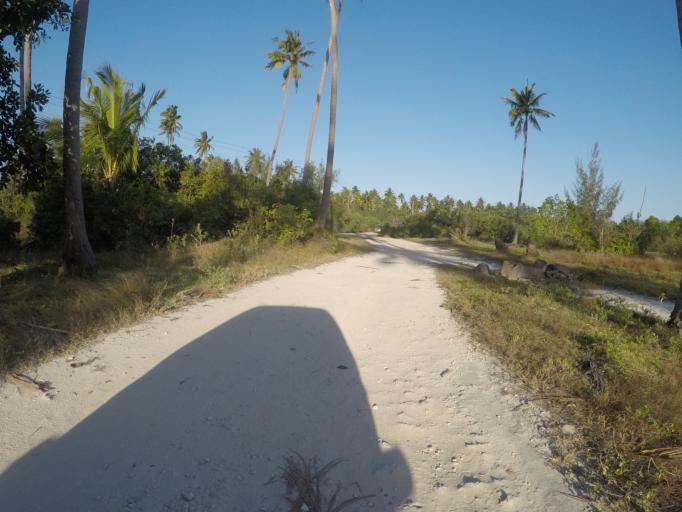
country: TZ
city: Kiwengwa
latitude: -6.1435
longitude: 39.4926
